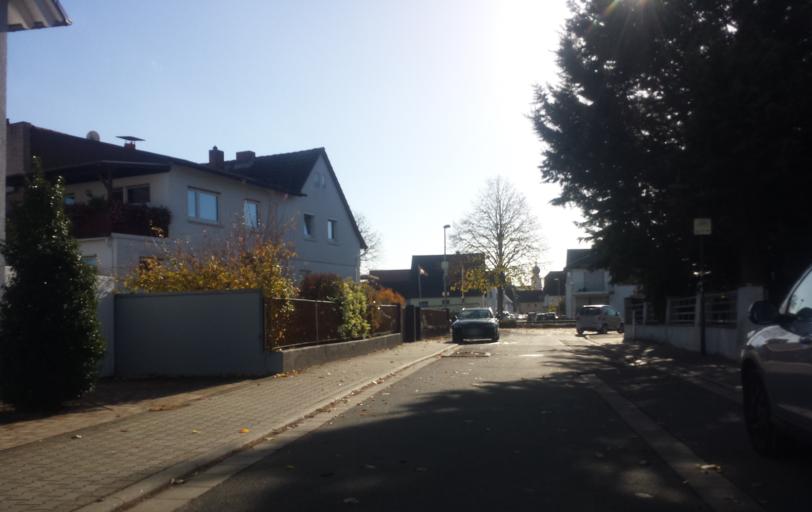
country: DE
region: Hesse
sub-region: Regierungsbezirk Darmstadt
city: Burstadt
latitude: 49.6467
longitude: 8.4515
